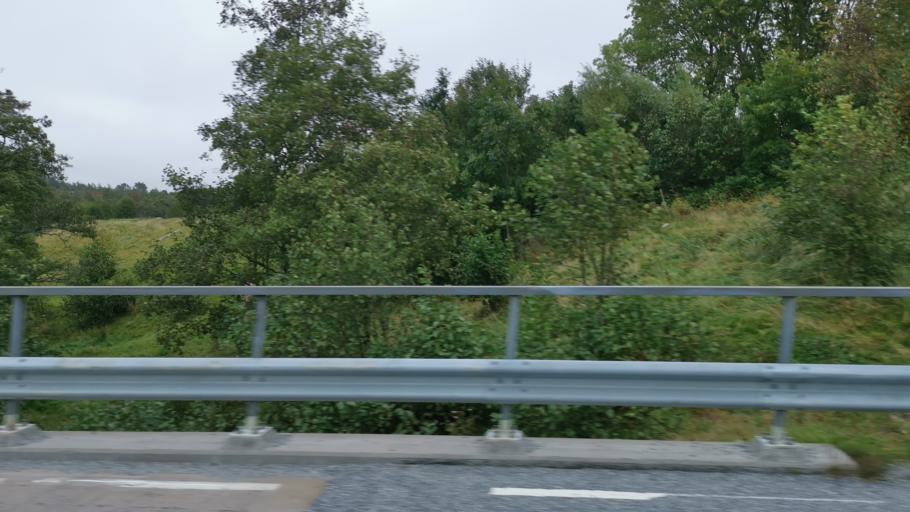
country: SE
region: Vaestra Goetaland
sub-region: Tanums Kommun
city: Tanumshede
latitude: 58.6398
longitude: 11.3409
